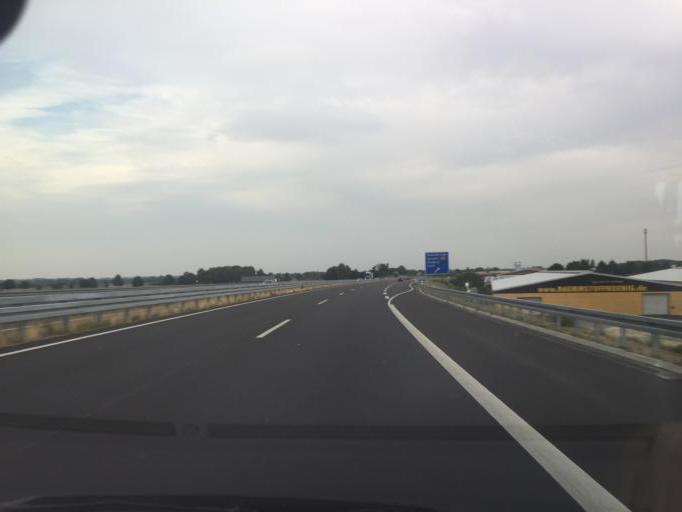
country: NL
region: Limburg
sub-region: Gemeente Venlo
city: Venlo
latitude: 51.3330
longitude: 6.2048
